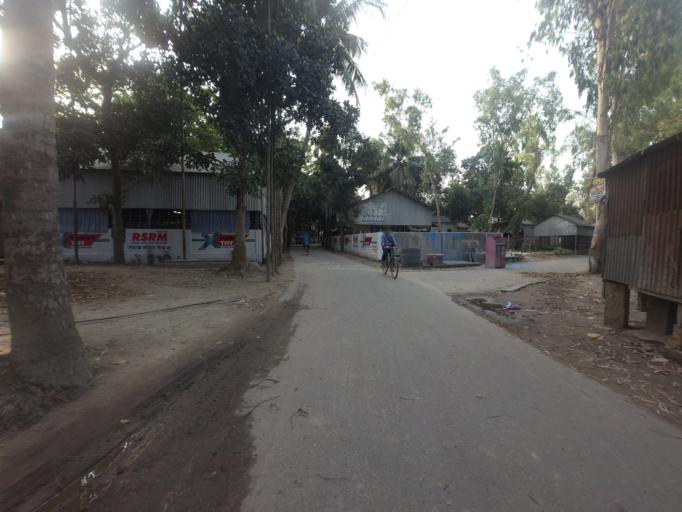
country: BD
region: Rajshahi
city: Sirajganj
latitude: 24.3200
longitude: 89.6943
